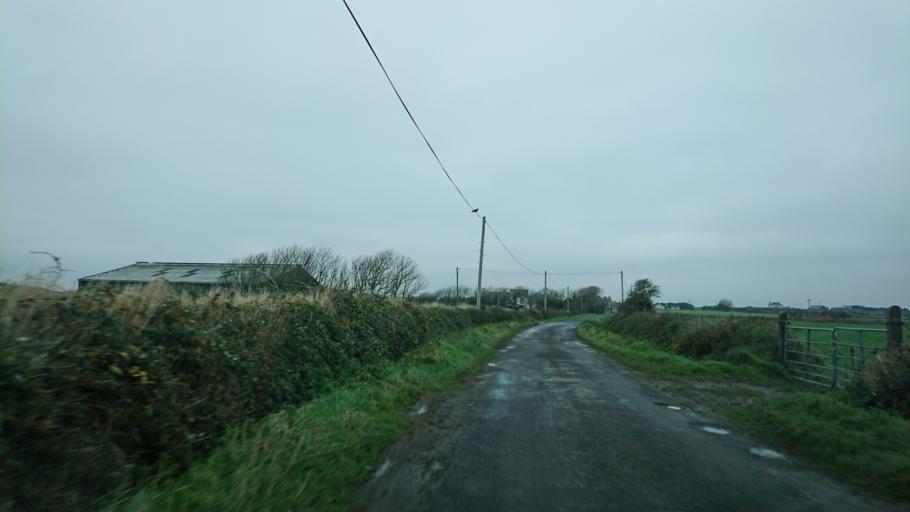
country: IE
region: Munster
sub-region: Waterford
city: Dunmore East
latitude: 52.1543
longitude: -7.0432
